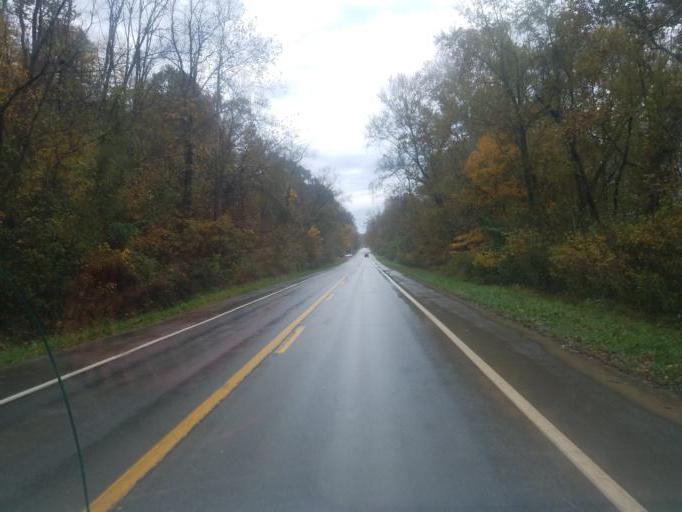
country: US
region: West Virginia
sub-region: Wood County
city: Williamstown
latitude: 39.3830
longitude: -81.4757
